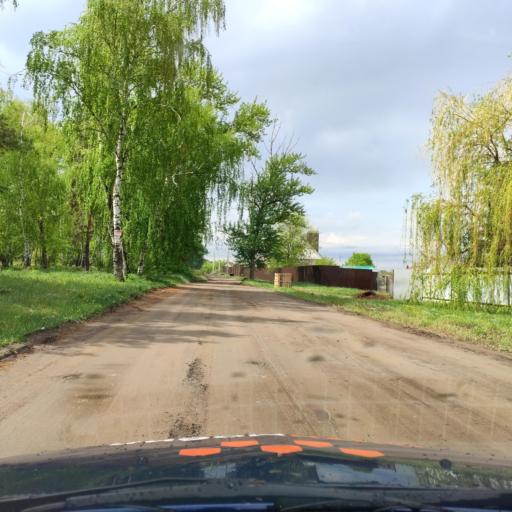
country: RU
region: Voronezj
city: Maslovka
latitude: 51.5509
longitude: 39.1987
